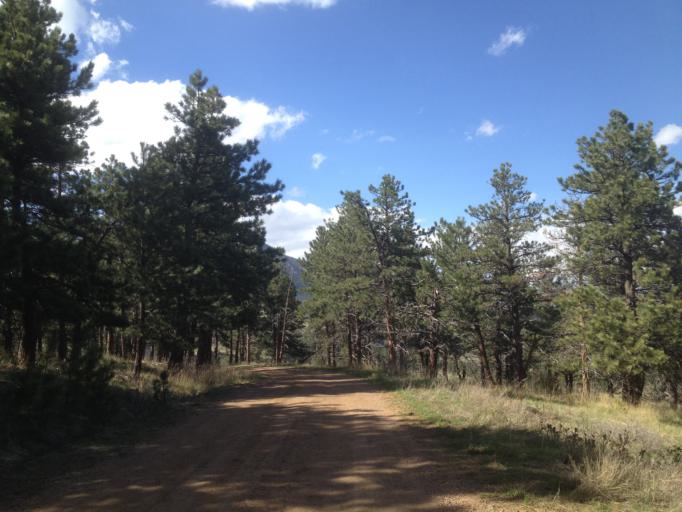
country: US
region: Colorado
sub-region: Boulder County
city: Boulder
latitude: 39.9223
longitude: -105.2714
